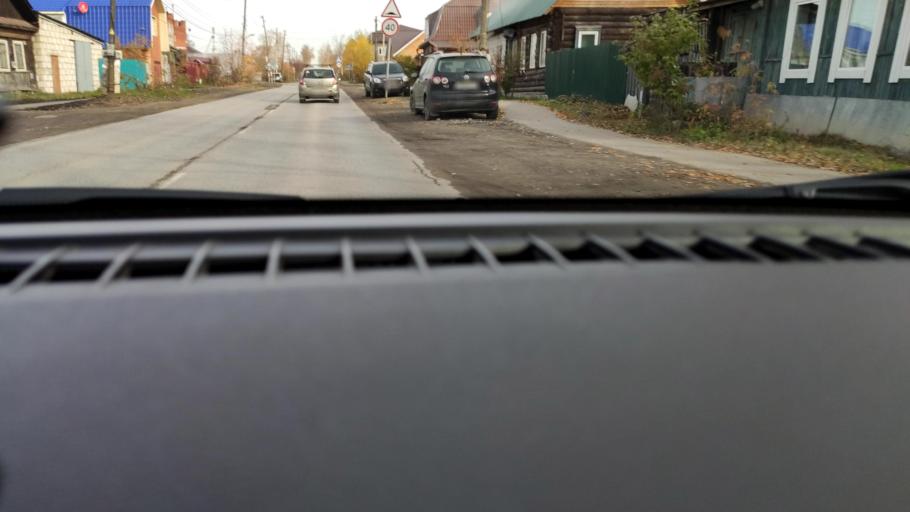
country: RU
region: Perm
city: Perm
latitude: 58.0440
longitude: 56.3281
